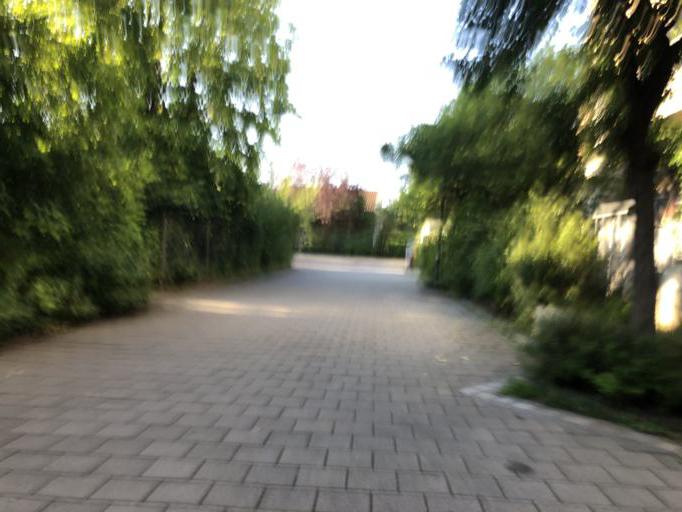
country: DE
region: Bavaria
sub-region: Regierungsbezirk Mittelfranken
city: Erlangen
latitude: 49.5950
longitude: 10.9611
